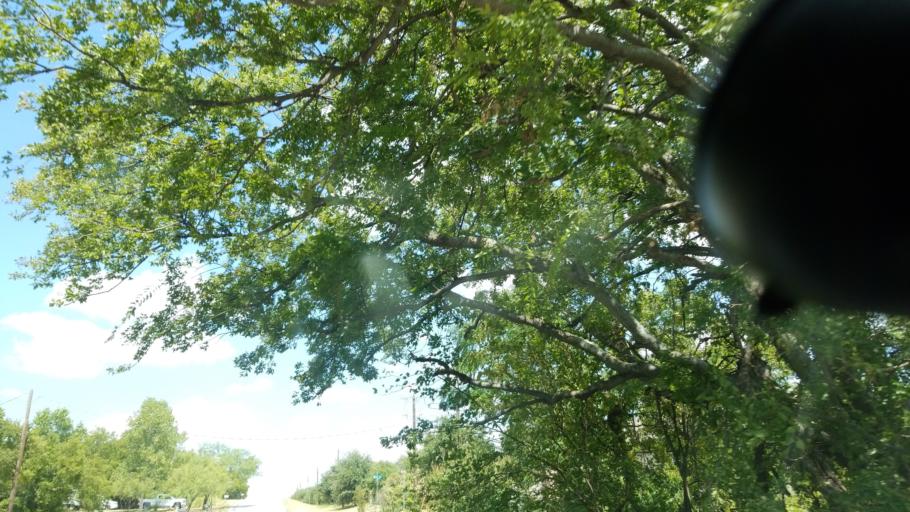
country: US
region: Texas
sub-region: Dallas County
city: Grand Prairie
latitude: 32.7211
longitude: -96.9772
